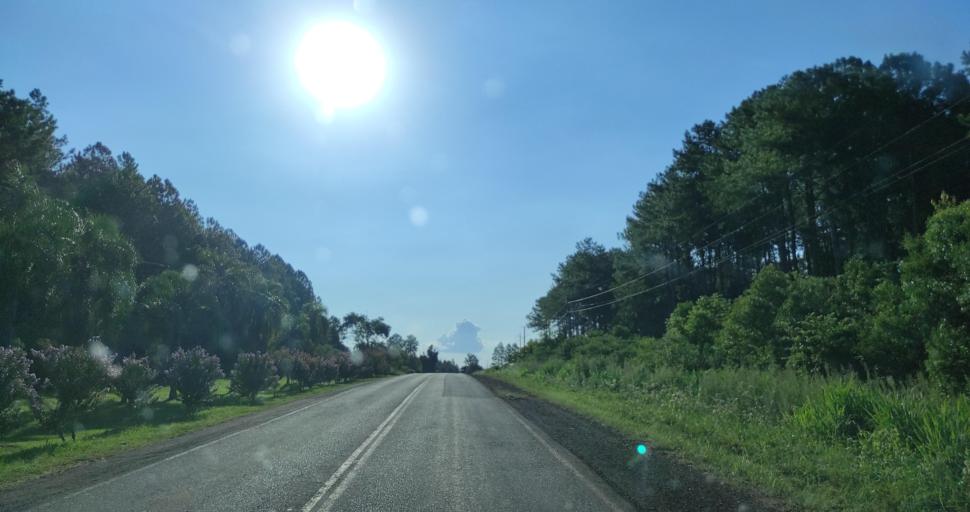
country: AR
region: Misiones
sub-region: Departamento de Eldorado
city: Eldorado
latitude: -26.4058
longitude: -54.4412
